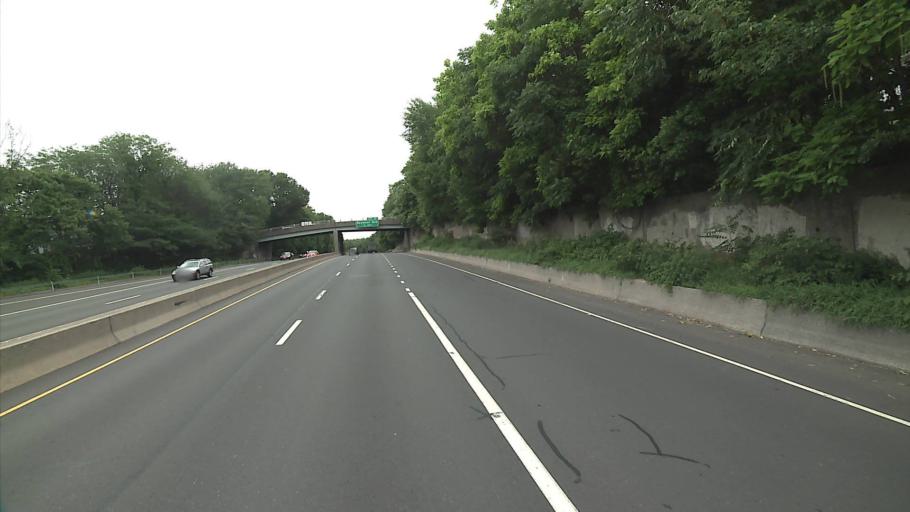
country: US
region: Connecticut
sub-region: New Haven County
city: Ansonia
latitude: 41.3375
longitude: -73.0924
